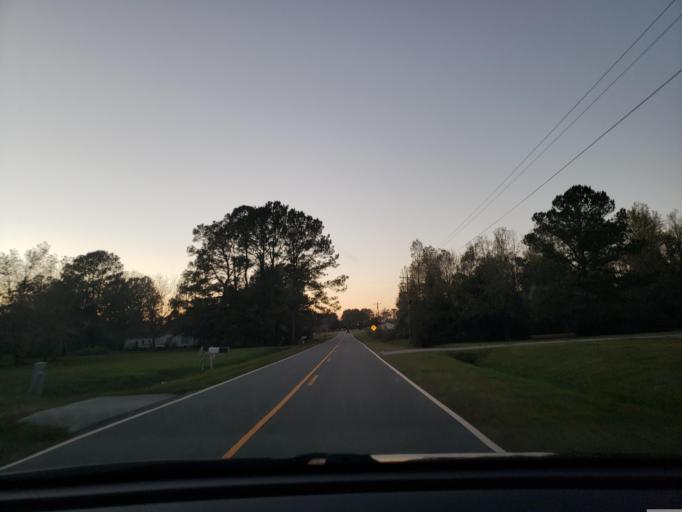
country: US
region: North Carolina
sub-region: Duplin County
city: Beulaville
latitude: 34.7932
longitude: -77.7662
